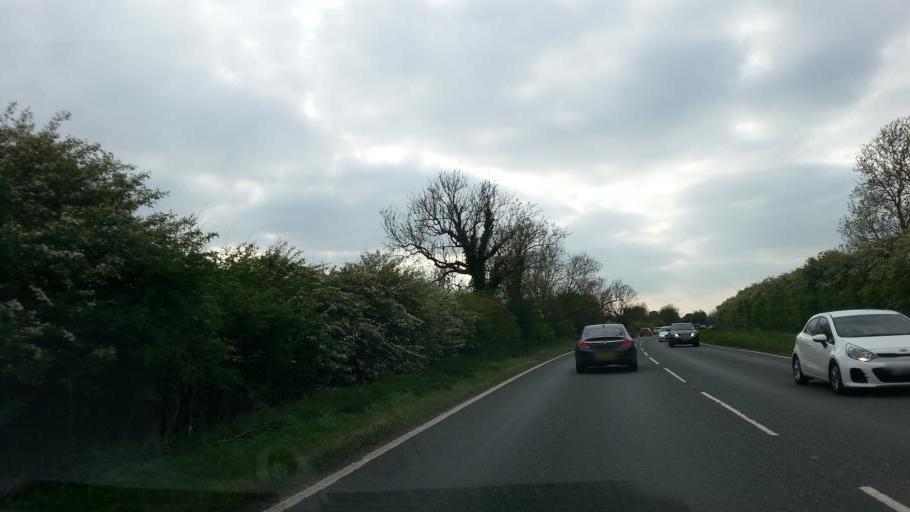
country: GB
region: England
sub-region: Nottinghamshire
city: South Collingham
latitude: 53.0708
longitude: -0.6797
